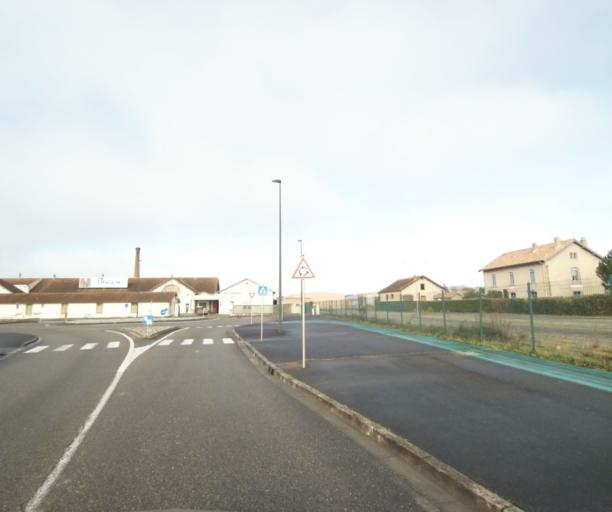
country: FR
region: Midi-Pyrenees
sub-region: Departement de la Haute-Garonne
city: Villemur-sur-Tarn
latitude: 43.8596
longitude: 1.4997
